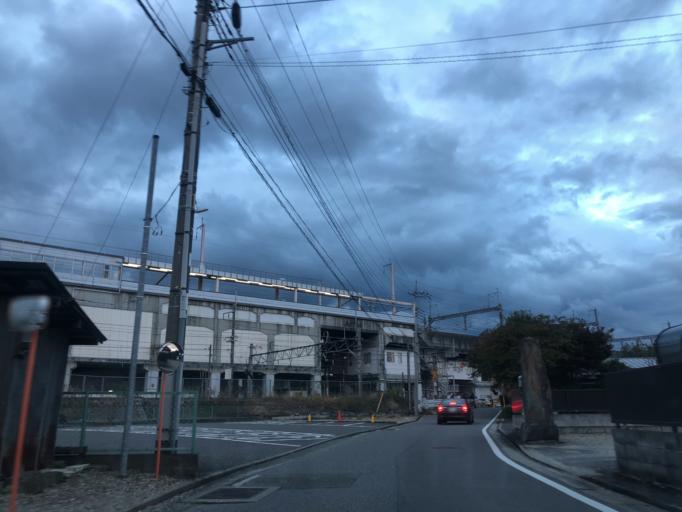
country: JP
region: Tochigi
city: Kuroiso
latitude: 36.9321
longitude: 140.0223
